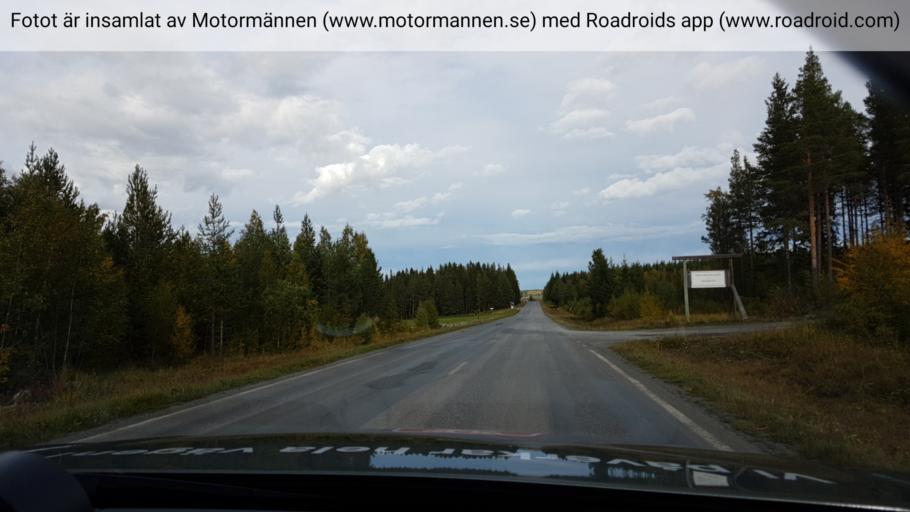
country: SE
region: Jaemtland
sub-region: OEstersunds Kommun
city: Ostersund
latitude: 63.1475
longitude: 14.4858
